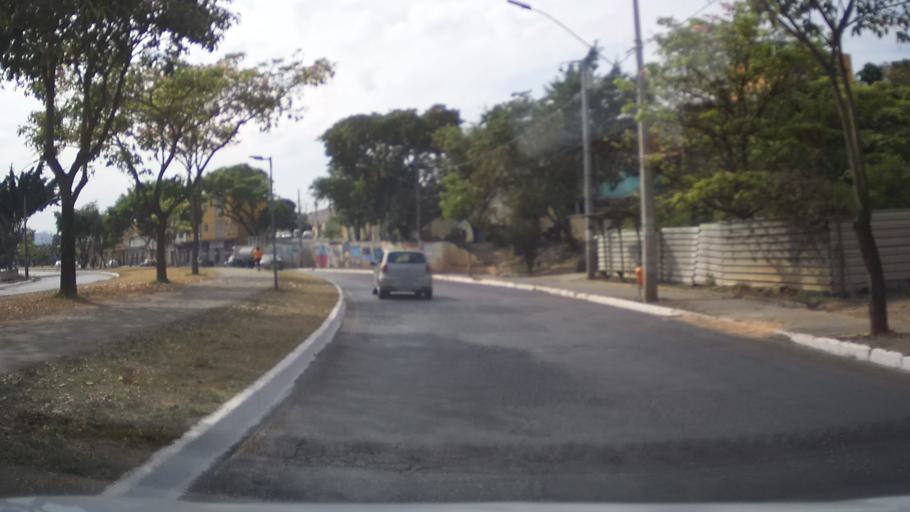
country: BR
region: Minas Gerais
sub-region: Contagem
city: Contagem
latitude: -19.9477
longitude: -44.0443
